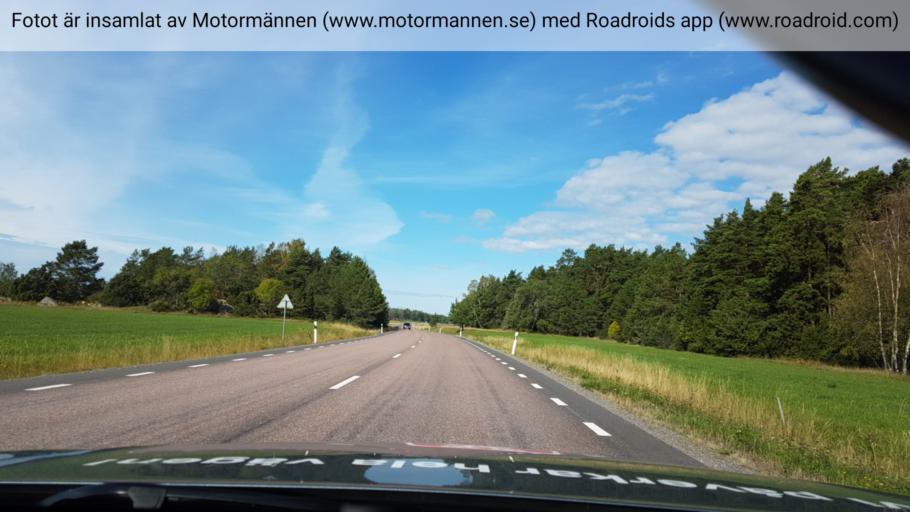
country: SE
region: Uppsala
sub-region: Osthammars Kommun
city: Bjorklinge
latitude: 59.9331
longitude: 17.4808
